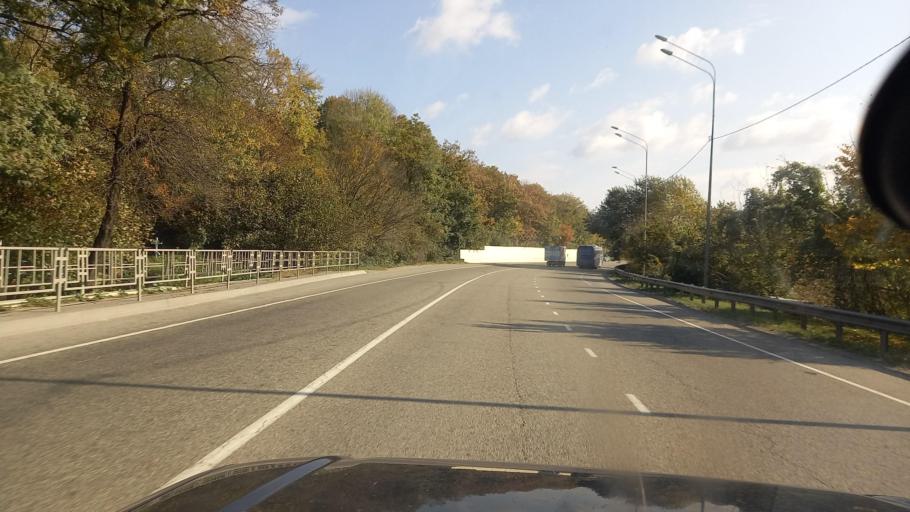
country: RU
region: Krasnodarskiy
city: Verkhnebakanskiy
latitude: 44.8694
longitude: 37.7484
